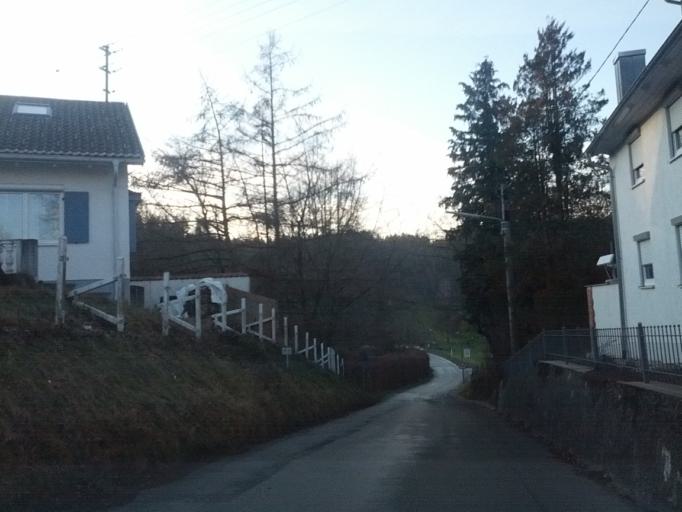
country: DE
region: Bavaria
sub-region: Swabia
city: Woringen
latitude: 47.8732
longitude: 10.2179
